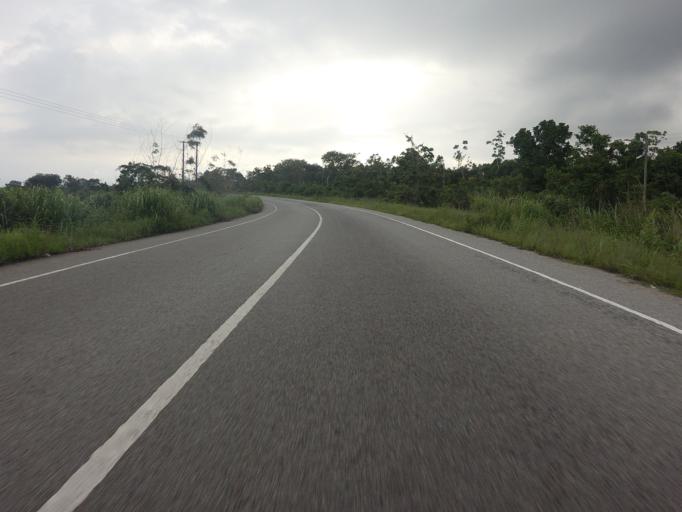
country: GH
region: Volta
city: Ho
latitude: 6.7864
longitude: 0.4537
